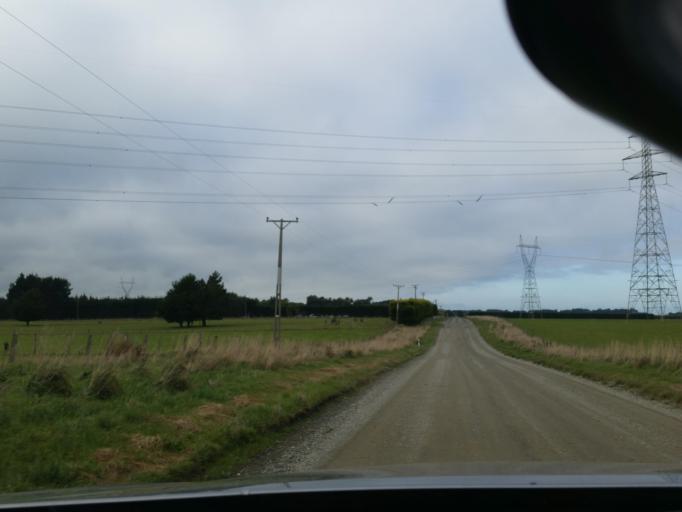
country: NZ
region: Southland
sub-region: Invercargill City
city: Invercargill
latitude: -46.3572
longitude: 168.4227
